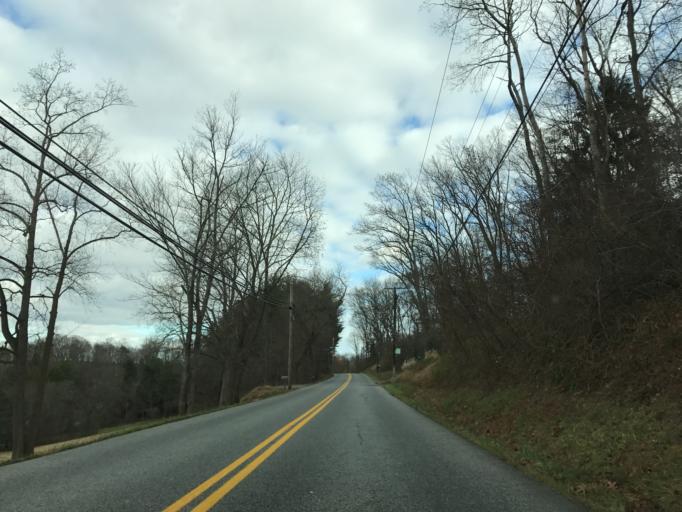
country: US
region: Pennsylvania
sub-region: York County
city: New Freedom
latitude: 39.6264
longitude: -76.6435
